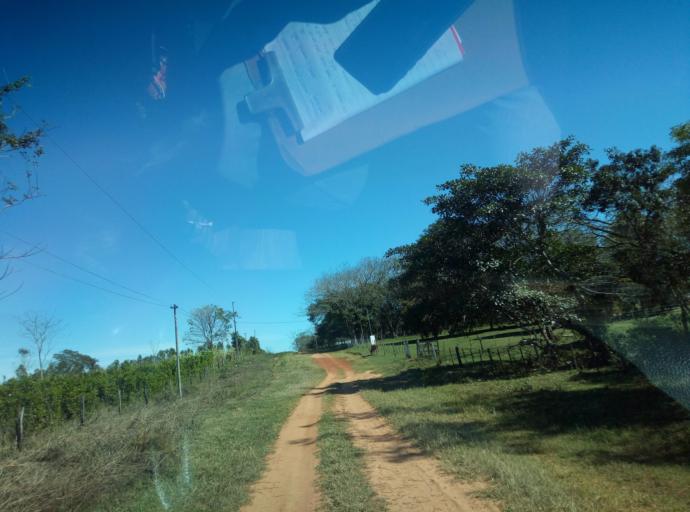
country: PY
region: Caaguazu
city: Doctor Cecilio Baez
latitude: -25.1789
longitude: -56.2444
